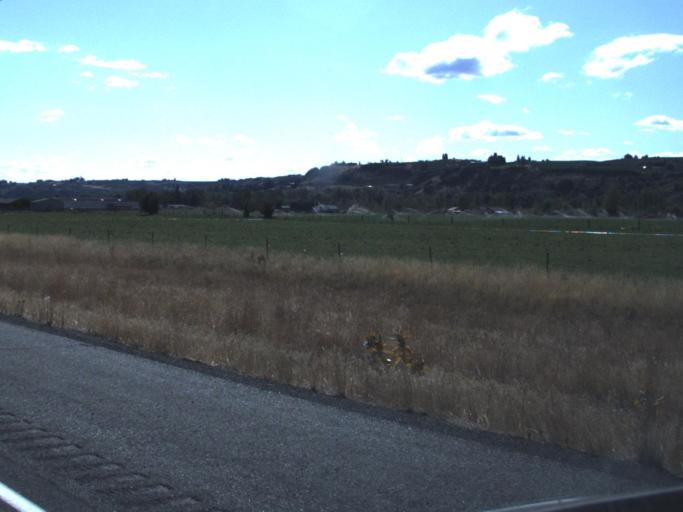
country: US
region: Washington
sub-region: Yakima County
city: Gleed
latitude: 46.6718
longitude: -120.6350
